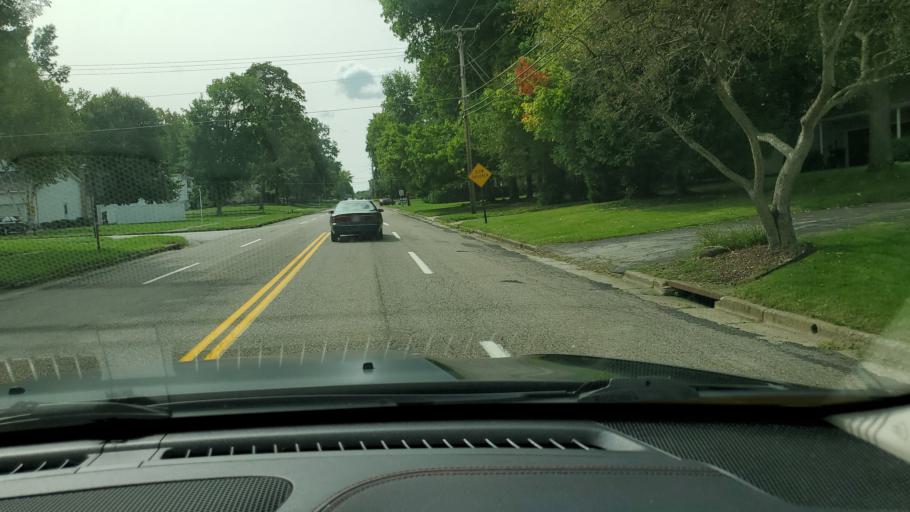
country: US
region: Ohio
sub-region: Mahoning County
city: Boardman
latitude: 41.0034
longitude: -80.6723
